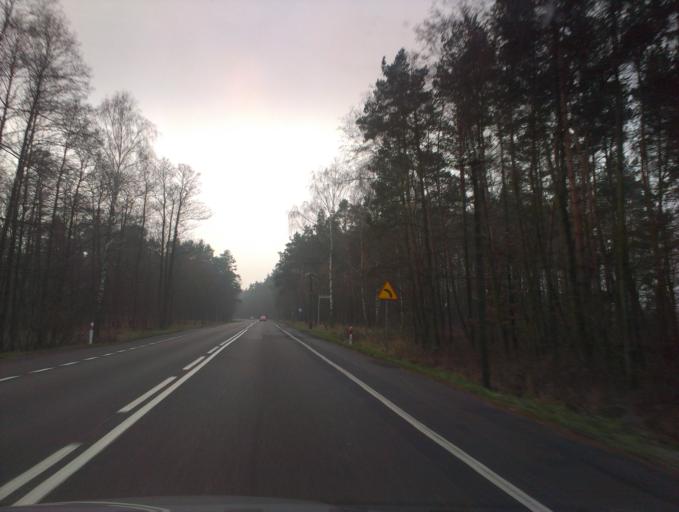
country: PL
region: Greater Poland Voivodeship
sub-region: Powiat chodzieski
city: Budzyn
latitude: 52.8487
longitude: 16.9706
